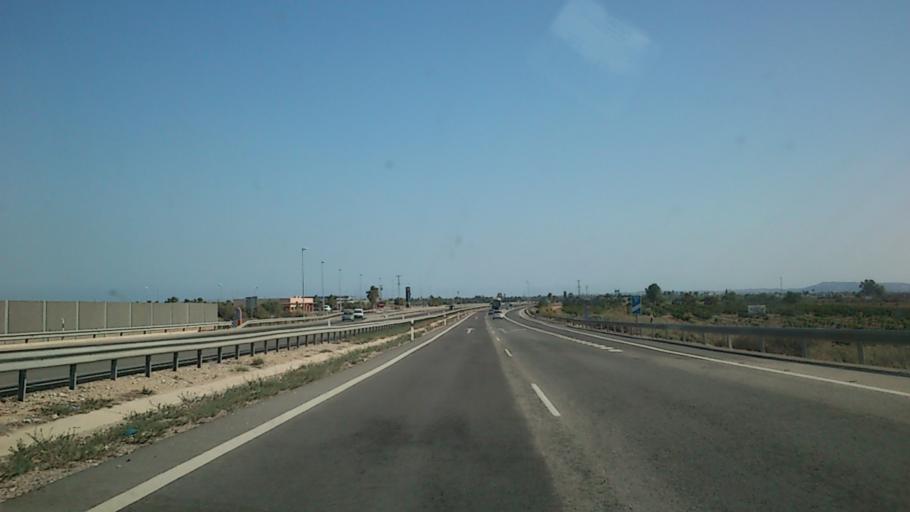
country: ES
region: Valencia
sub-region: Provincia de Alicante
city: San Isidro
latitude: 38.1993
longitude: -0.8147
